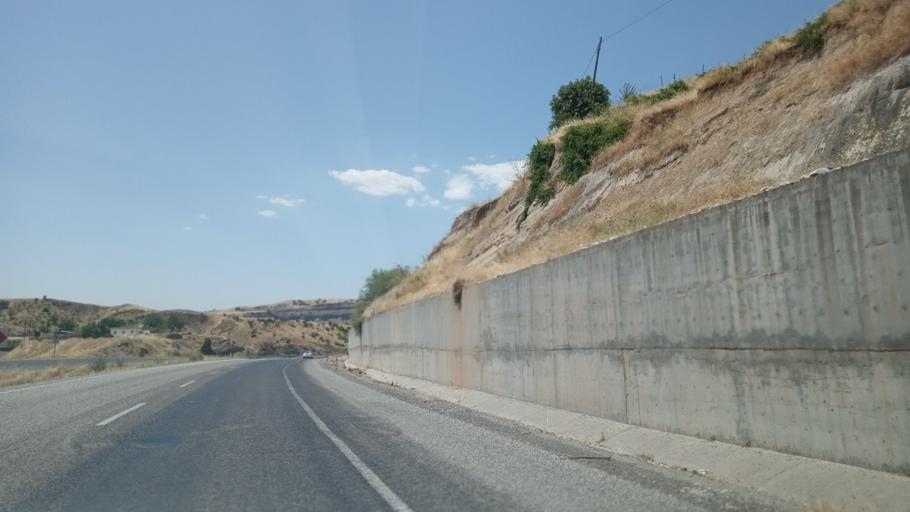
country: TR
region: Batman
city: Kozluk
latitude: 38.1515
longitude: 41.4079
